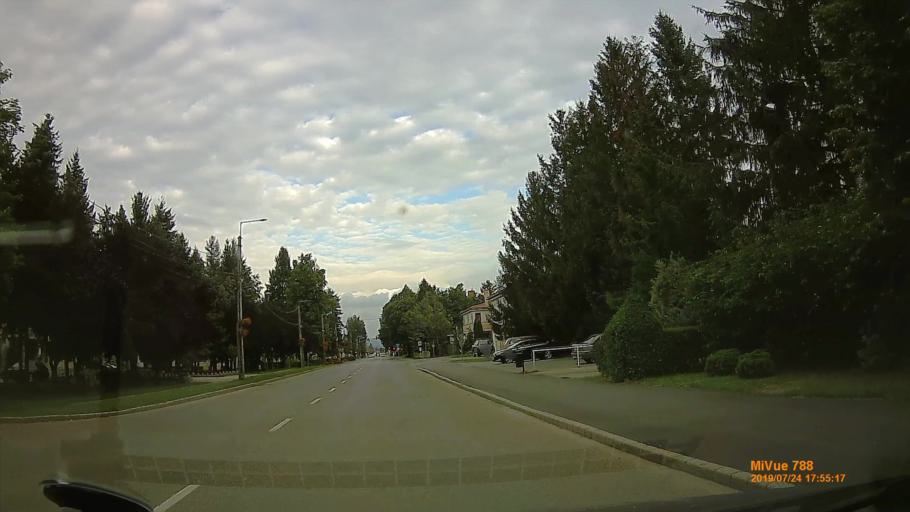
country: HU
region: Borsod-Abauj-Zemplen
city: Encs
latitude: 48.3342
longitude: 21.1115
